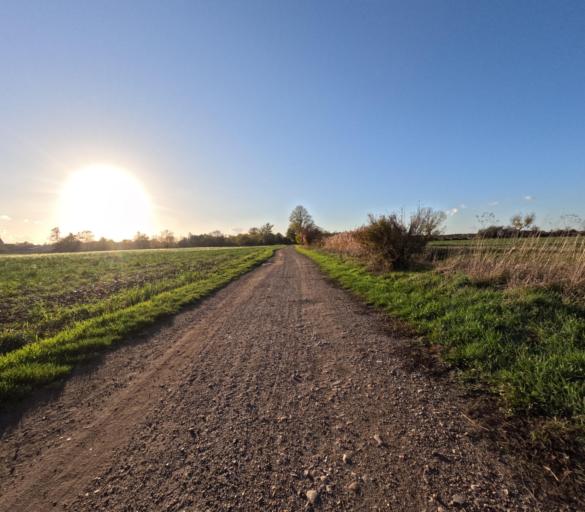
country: DE
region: Saxony-Anhalt
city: Zoschen
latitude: 51.3639
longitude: 12.1216
